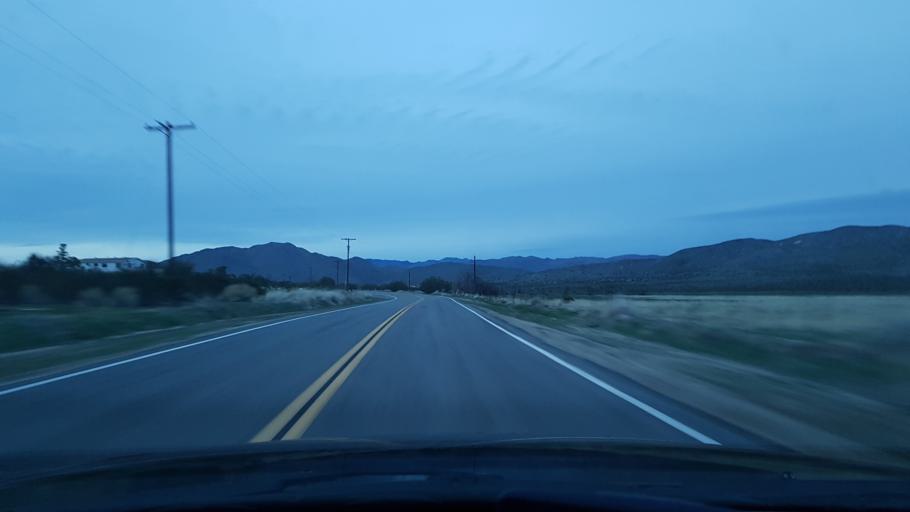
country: US
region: California
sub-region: San Diego County
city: Julian
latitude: 33.0643
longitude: -116.4275
